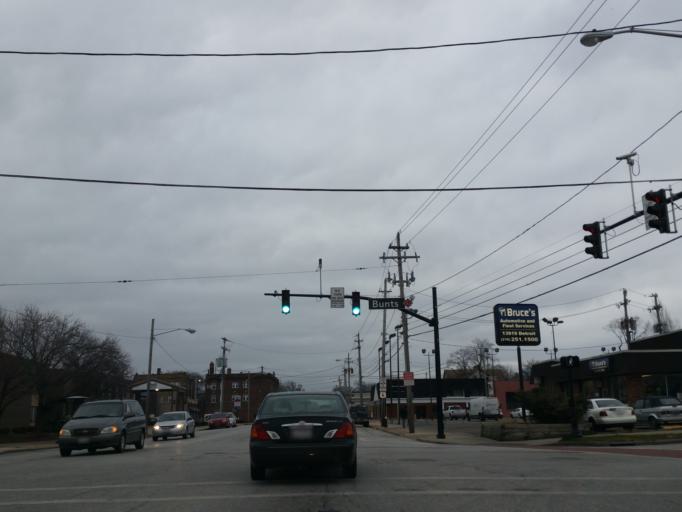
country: US
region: Ohio
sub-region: Cuyahoga County
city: Lakewood
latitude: 41.4855
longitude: -81.7897
